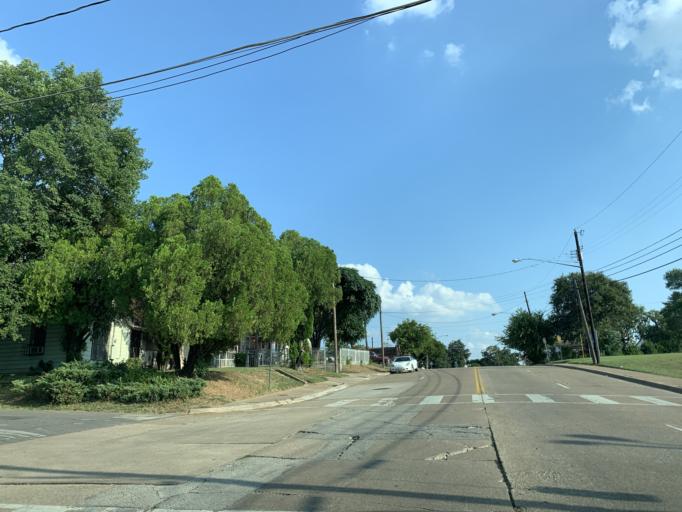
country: US
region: Texas
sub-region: Dallas County
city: Dallas
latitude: 32.7418
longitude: -96.7943
